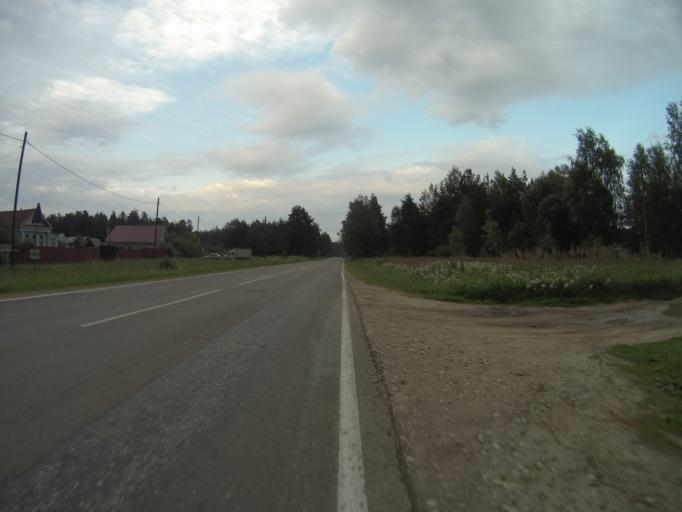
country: RU
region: Vladimir
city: Kameshkovo
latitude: 56.3516
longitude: 40.9252
